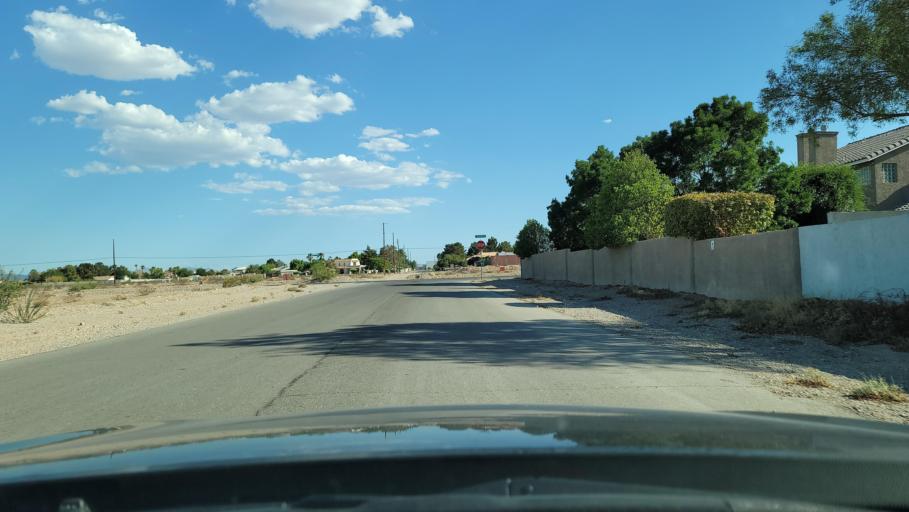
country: US
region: Nevada
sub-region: Clark County
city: Spring Valley
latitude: 36.0823
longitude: -115.2318
